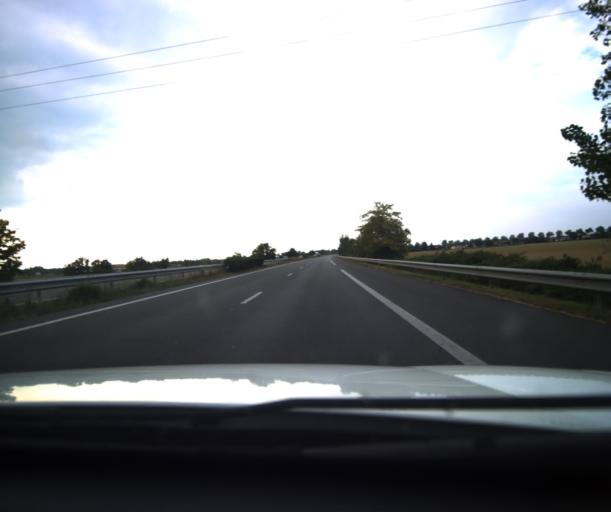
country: FR
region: Midi-Pyrenees
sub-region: Departement du Tarn-et-Garonne
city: Saint-Porquier
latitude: 44.0261
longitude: 1.1679
